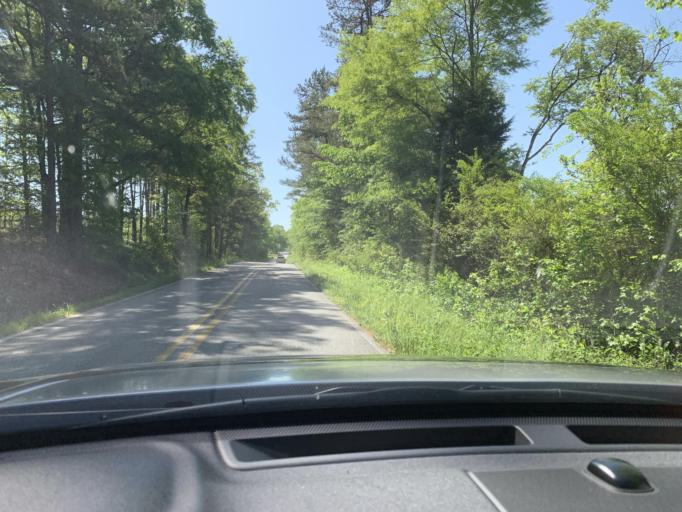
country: US
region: Georgia
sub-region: Polk County
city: Cedartown
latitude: 33.9408
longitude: -85.2130
